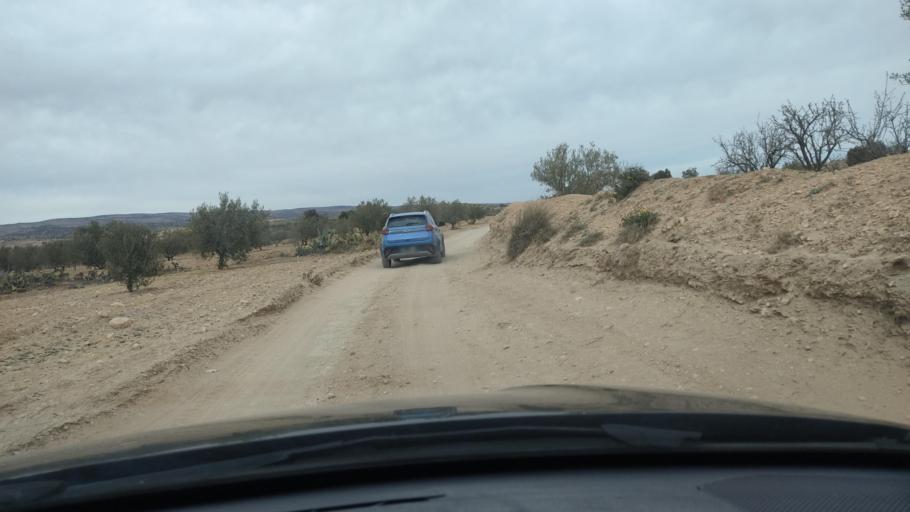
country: TN
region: Al Qasrayn
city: Kasserine
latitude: 35.2546
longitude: 8.9216
